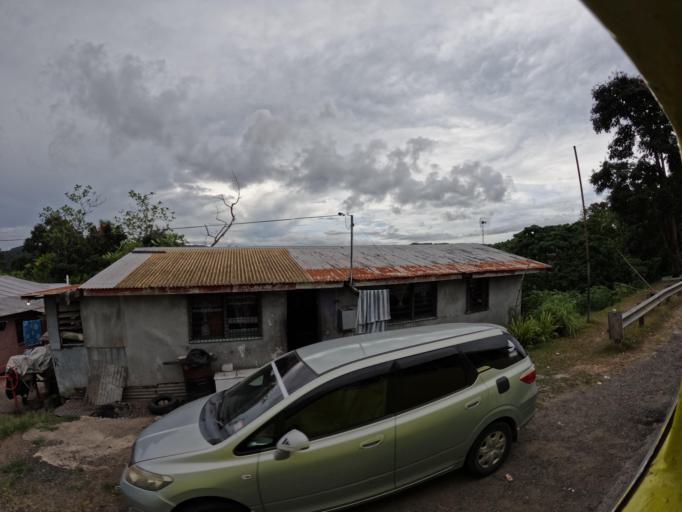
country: FJ
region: Central
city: Suva
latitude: -18.0845
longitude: 178.4530
